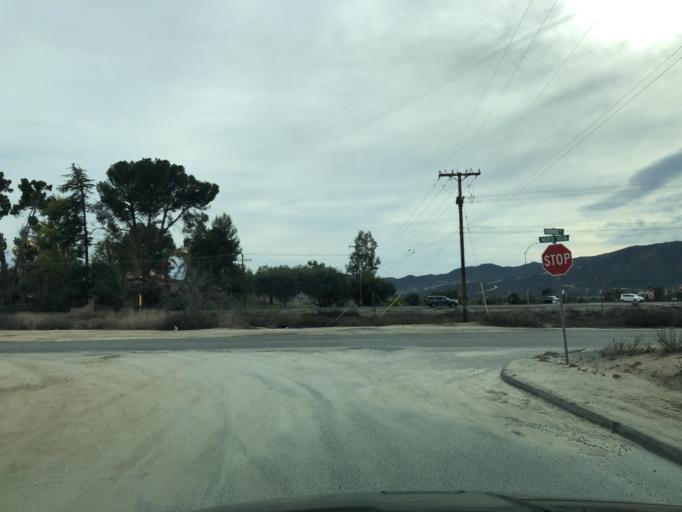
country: US
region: California
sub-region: Riverside County
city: Wildomar
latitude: 33.6132
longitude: -117.2581
